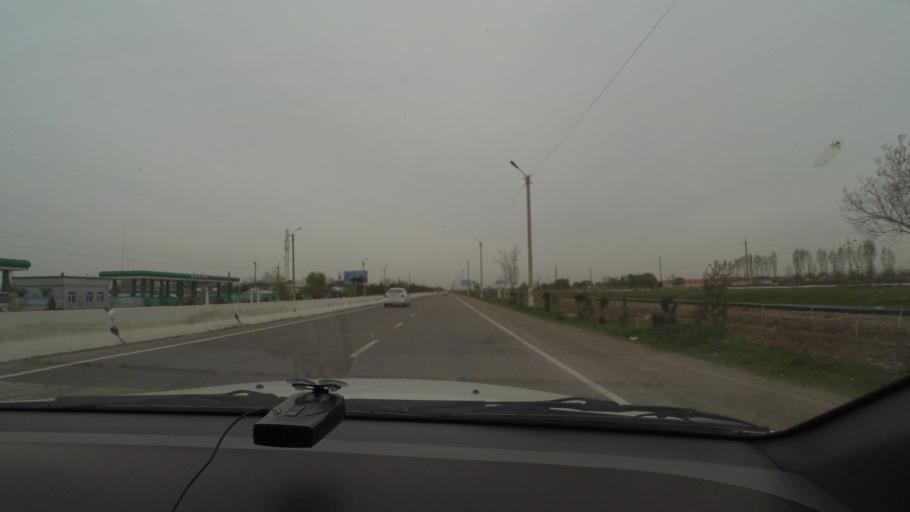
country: UZ
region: Sirdaryo
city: Guliston
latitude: 40.4887
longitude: 68.7450
